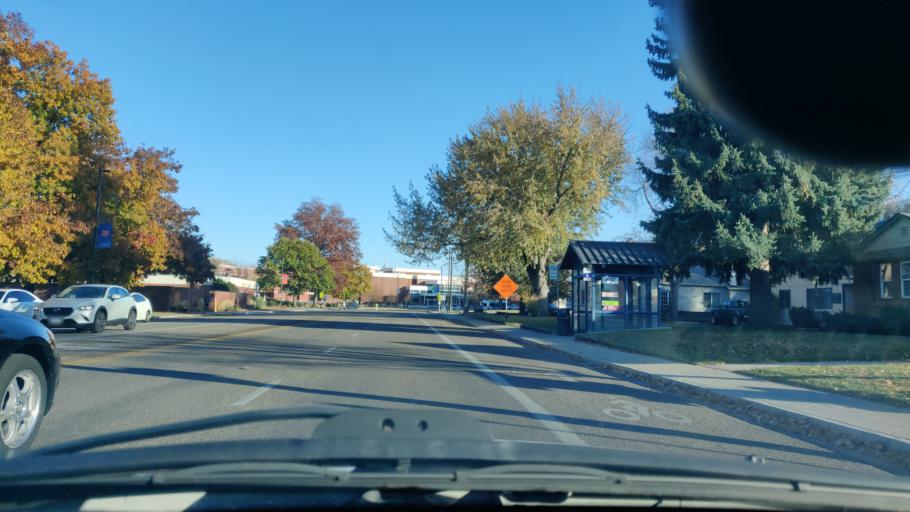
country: US
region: Idaho
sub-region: Ada County
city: Boise
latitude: 43.6028
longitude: -116.2045
